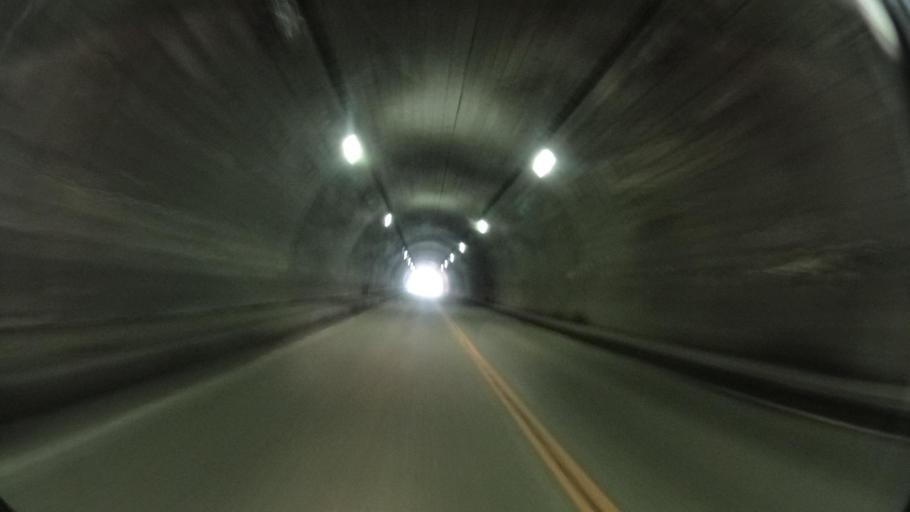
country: JP
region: Kyoto
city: Maizuru
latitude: 35.5027
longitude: 135.3835
